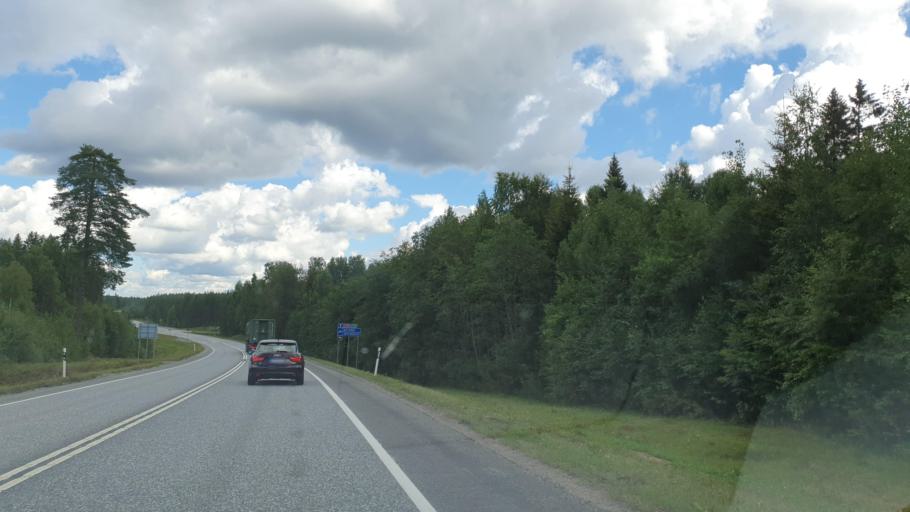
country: FI
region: Kainuu
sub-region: Kajaani
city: Kajaani
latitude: 64.1830
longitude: 27.5940
